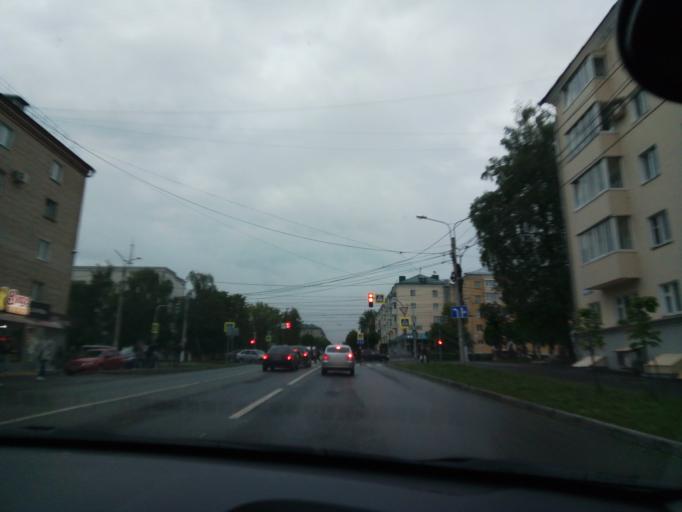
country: RU
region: Chuvashia
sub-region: Cheboksarskiy Rayon
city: Cheboksary
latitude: 56.1249
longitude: 47.2559
